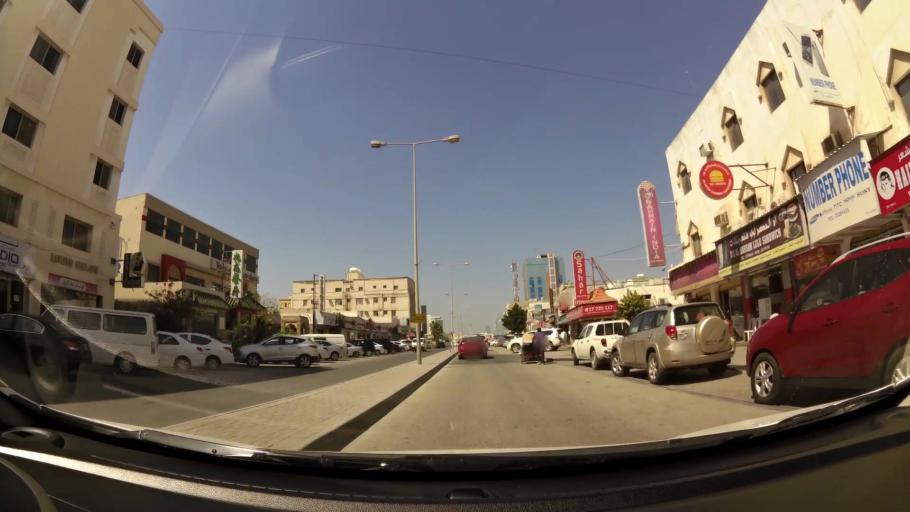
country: BH
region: Manama
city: Manama
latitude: 26.2046
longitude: 50.5963
